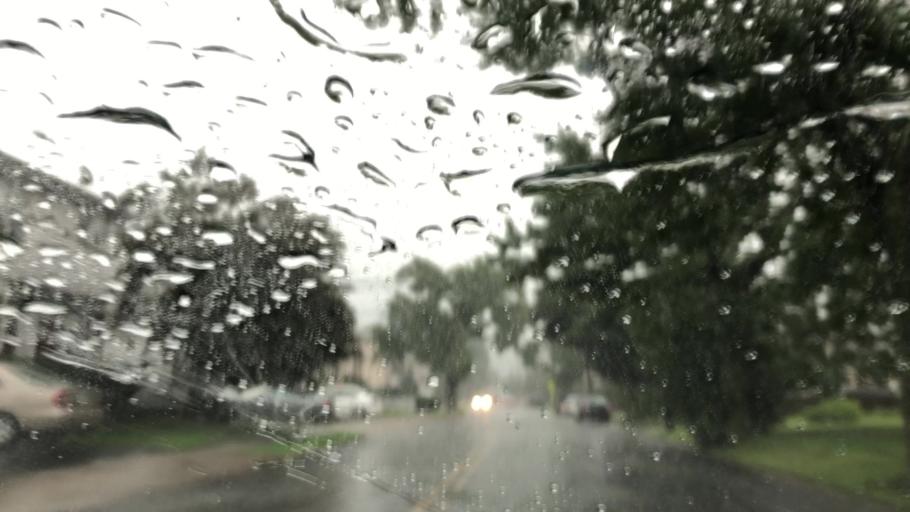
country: US
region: New Jersey
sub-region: Bergen County
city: Elmwood Park
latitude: 40.9091
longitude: -74.1139
